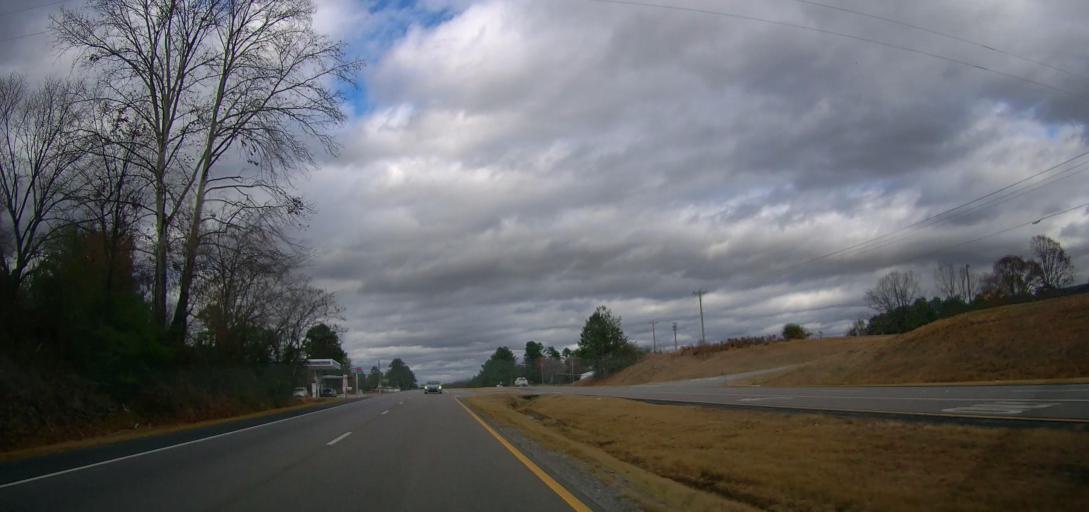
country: US
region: Alabama
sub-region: Morgan County
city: Falkville
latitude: 34.3008
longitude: -86.9972
